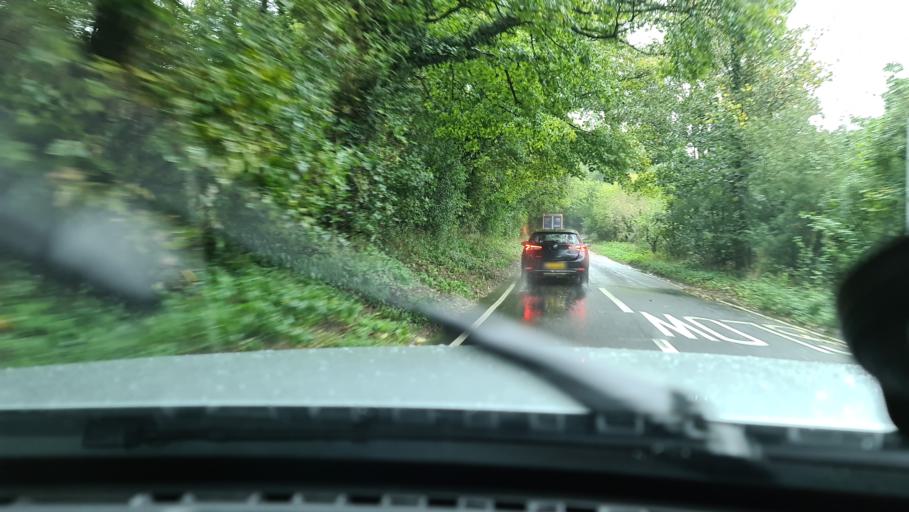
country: GB
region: England
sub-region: Oxfordshire
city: Woodstock
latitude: 51.8757
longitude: -1.3537
